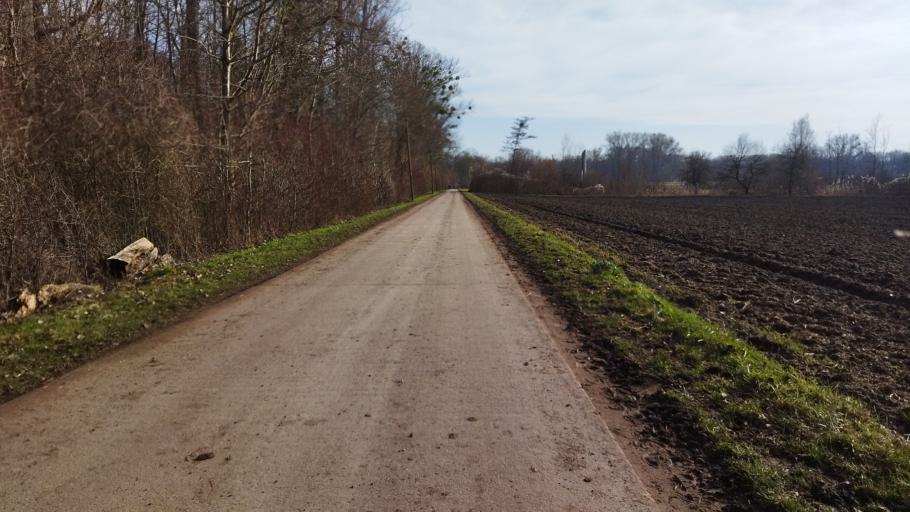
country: DE
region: Rheinland-Pfalz
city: Germersheim
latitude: 49.1872
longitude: 8.3702
